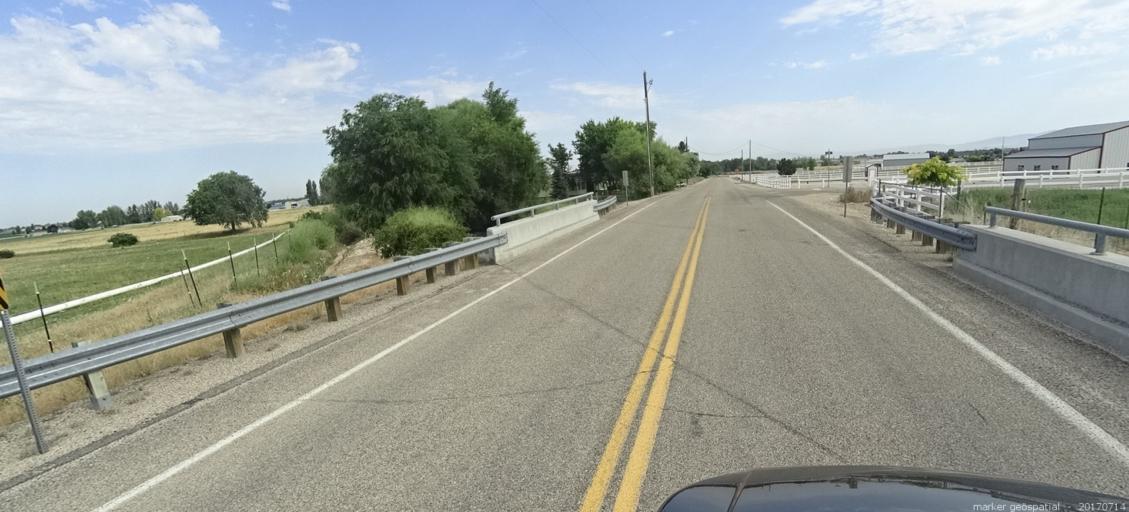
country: US
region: Idaho
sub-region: Ada County
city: Kuna
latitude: 43.4985
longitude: -116.3543
